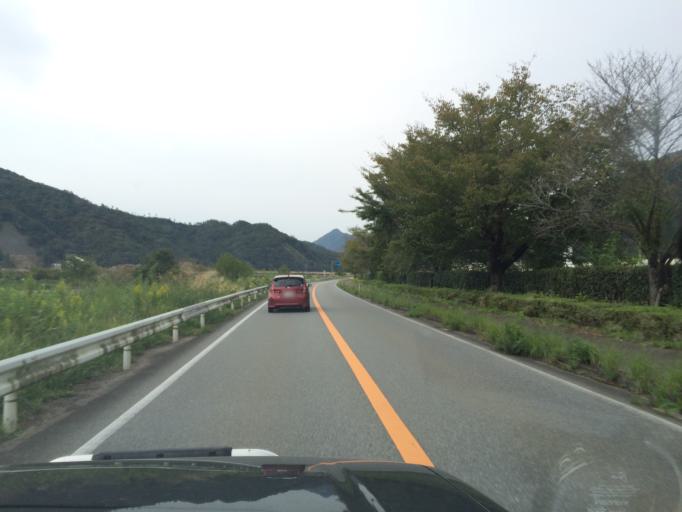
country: JP
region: Hyogo
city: Toyooka
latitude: 35.3908
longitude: 134.7983
